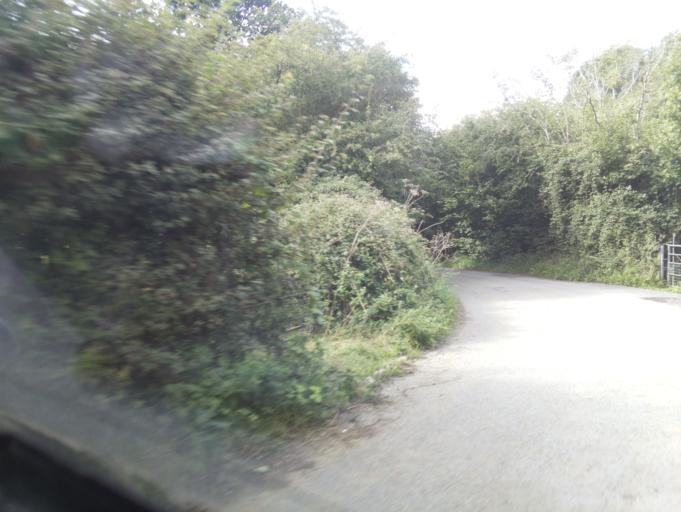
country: GB
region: England
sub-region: Wiltshire
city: Colerne
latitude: 51.4309
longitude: -2.2556
